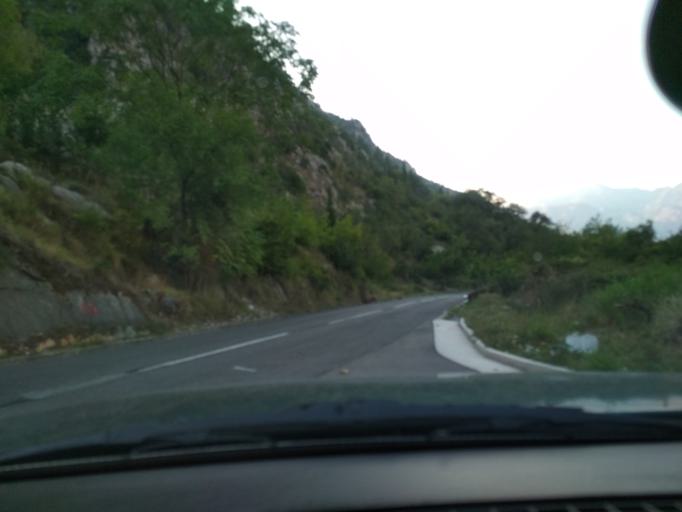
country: ME
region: Kotor
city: Kotor
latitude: 42.4189
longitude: 18.7591
